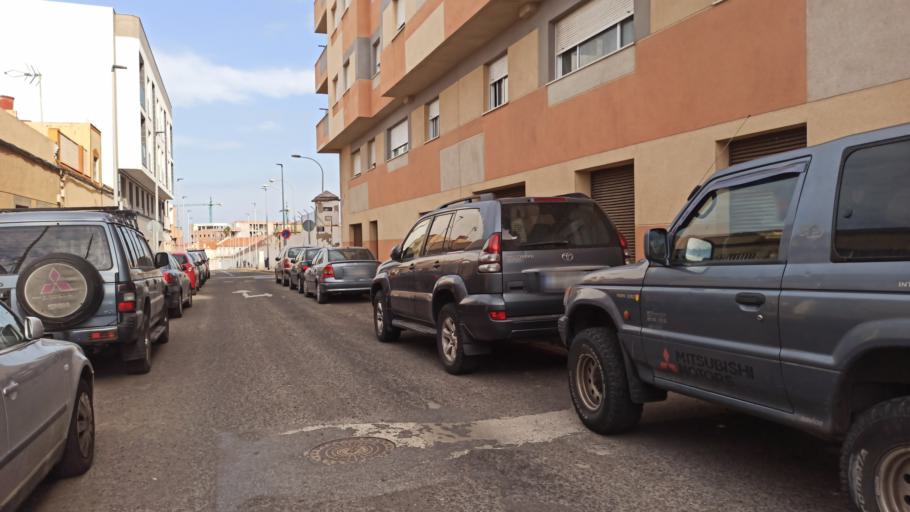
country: ES
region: Melilla
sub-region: Melilla
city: Melilla
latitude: 35.2827
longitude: -2.9482
